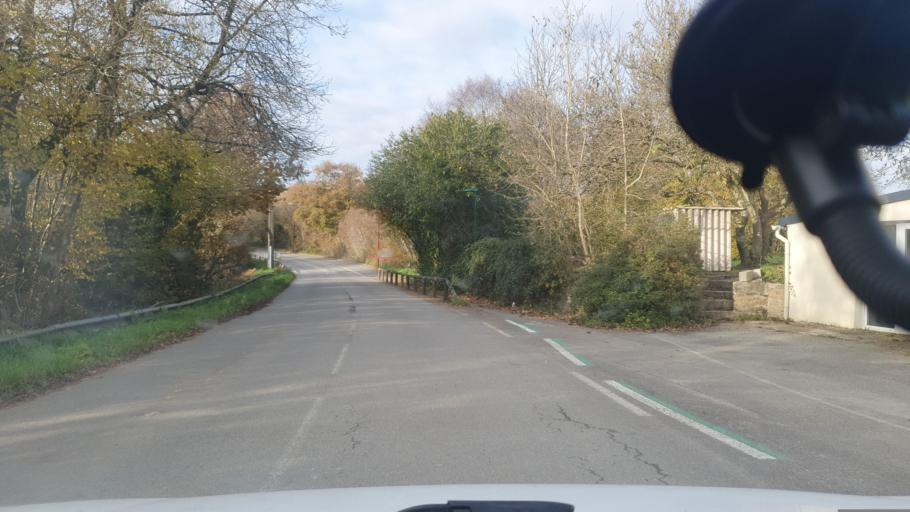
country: FR
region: Brittany
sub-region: Departement du Finistere
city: Edern
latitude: 48.1026
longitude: -3.9864
